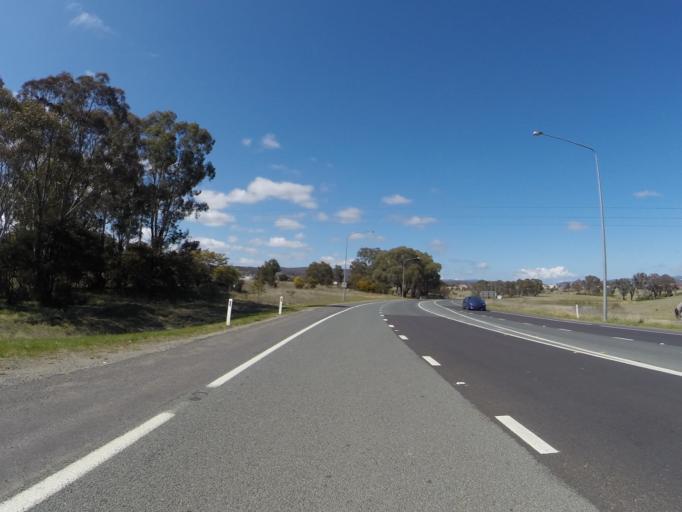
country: AU
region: New South Wales
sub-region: Queanbeyan
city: Queanbeyan
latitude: -35.3310
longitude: 149.2378
